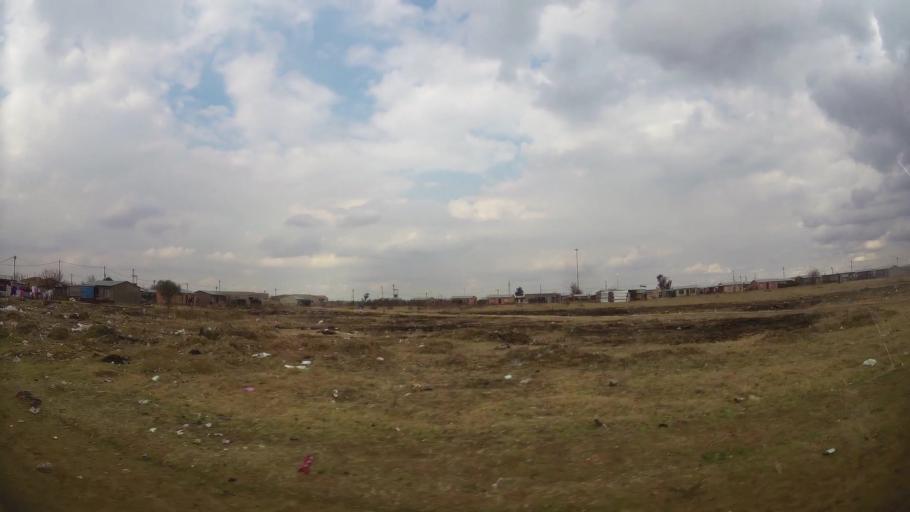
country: ZA
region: Orange Free State
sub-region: Fezile Dabi District Municipality
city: Sasolburg
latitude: -26.8603
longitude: 27.8659
